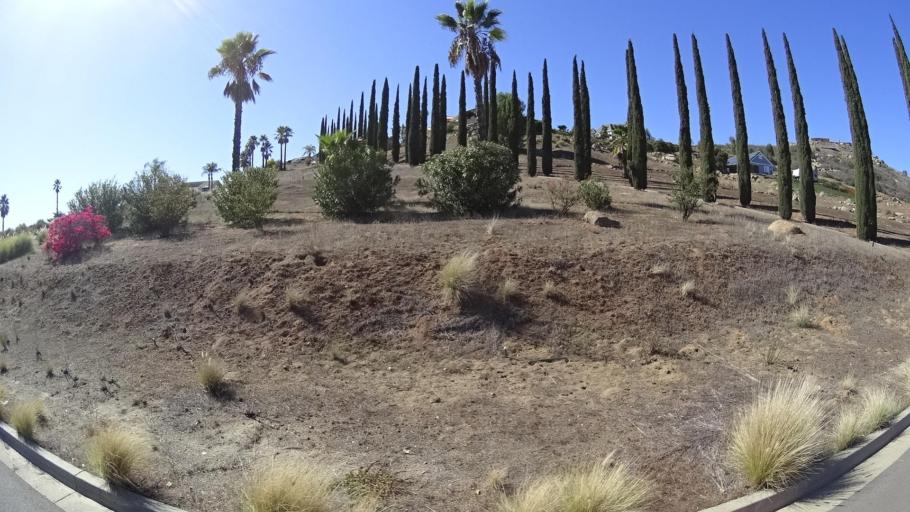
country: US
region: California
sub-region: San Diego County
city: Lakeside
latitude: 32.8691
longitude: -116.8672
